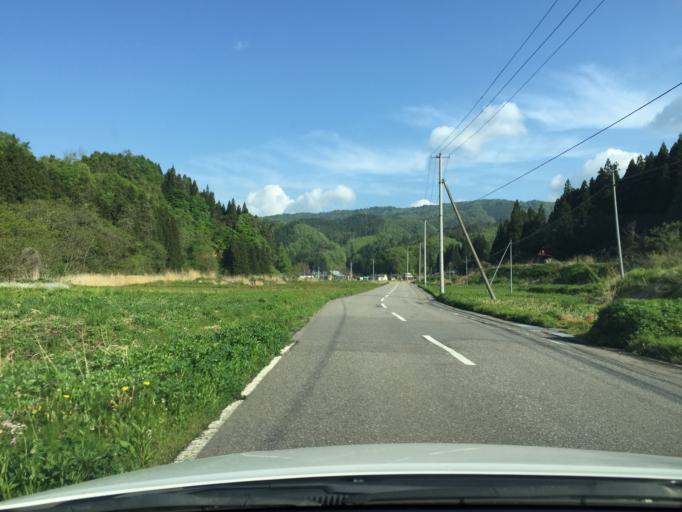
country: JP
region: Fukushima
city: Kitakata
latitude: 37.6600
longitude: 139.7558
